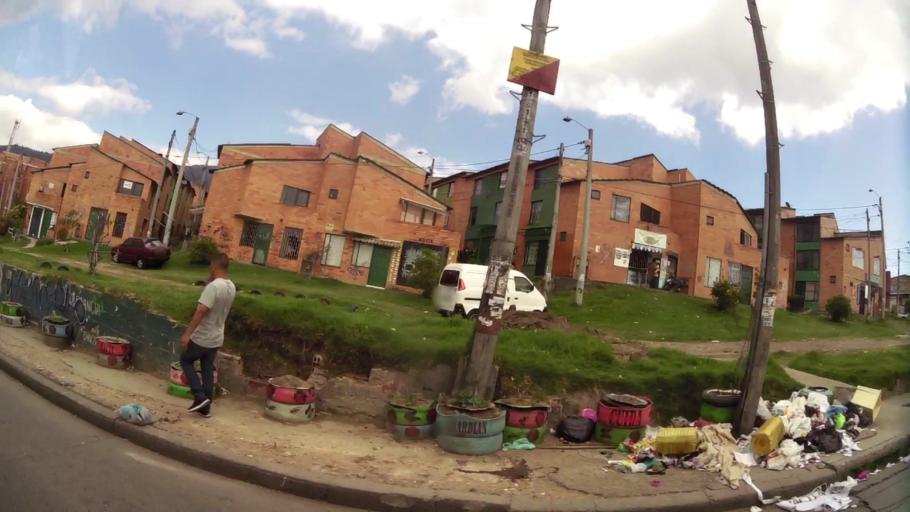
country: CO
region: Bogota D.C.
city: Bogota
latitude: 4.5550
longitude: -74.0916
